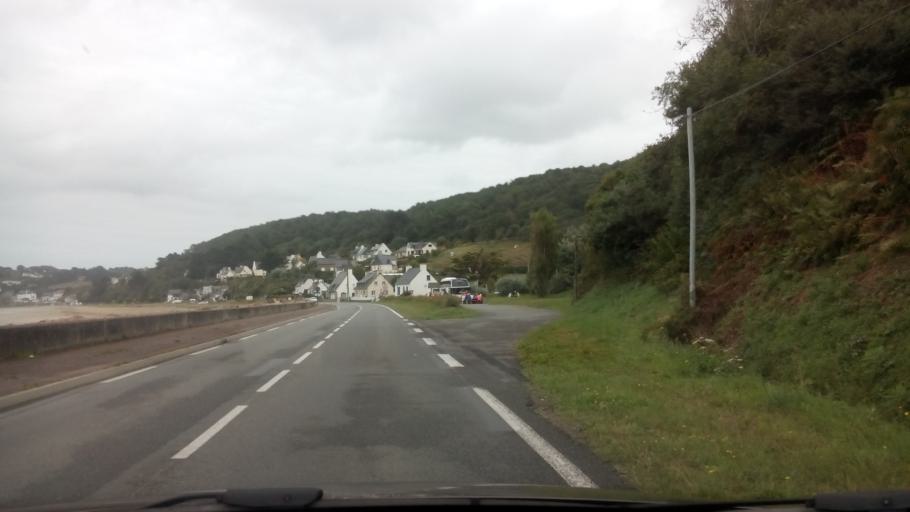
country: FR
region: Brittany
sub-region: Departement des Cotes-d'Armor
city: Locquemeau
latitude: 48.6743
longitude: -3.5740
